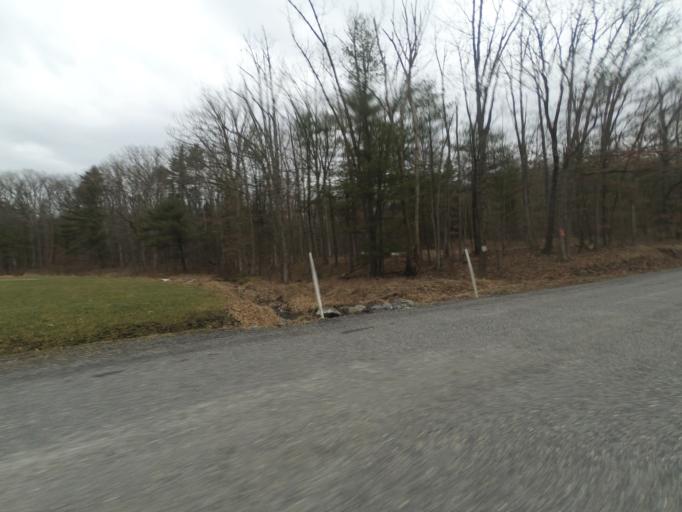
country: US
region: Pennsylvania
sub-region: Centre County
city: Stormstown
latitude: 40.8547
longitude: -77.9786
